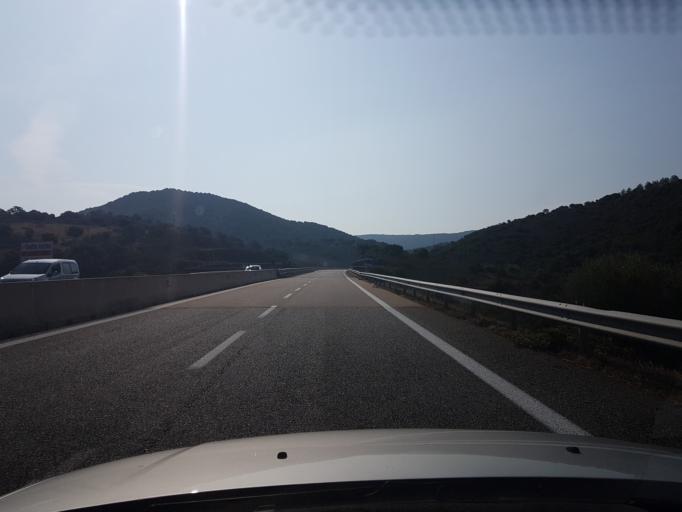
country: IT
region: Sardinia
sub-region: Provincia di Olbia-Tempio
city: Loiri Porto San Paolo
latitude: 40.8303
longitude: 9.5705
